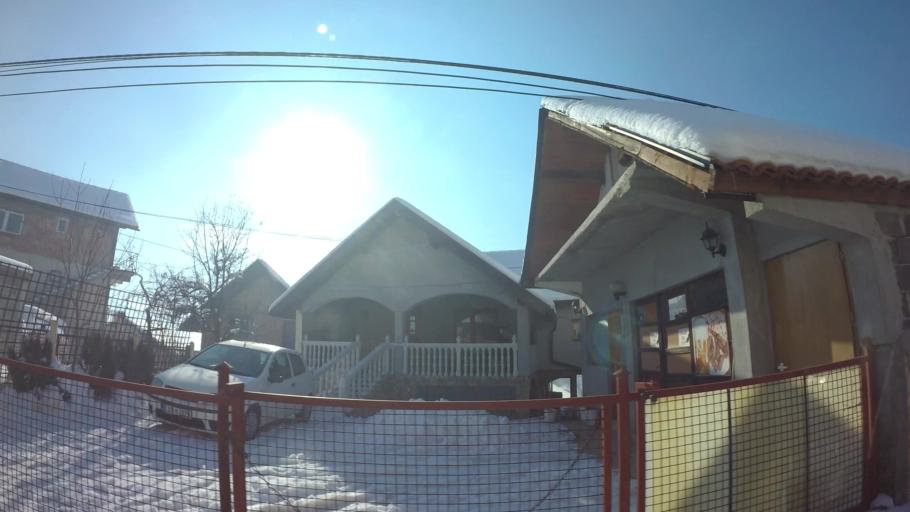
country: BA
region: Federation of Bosnia and Herzegovina
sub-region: Kanton Sarajevo
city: Sarajevo
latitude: 43.8392
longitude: 18.3713
